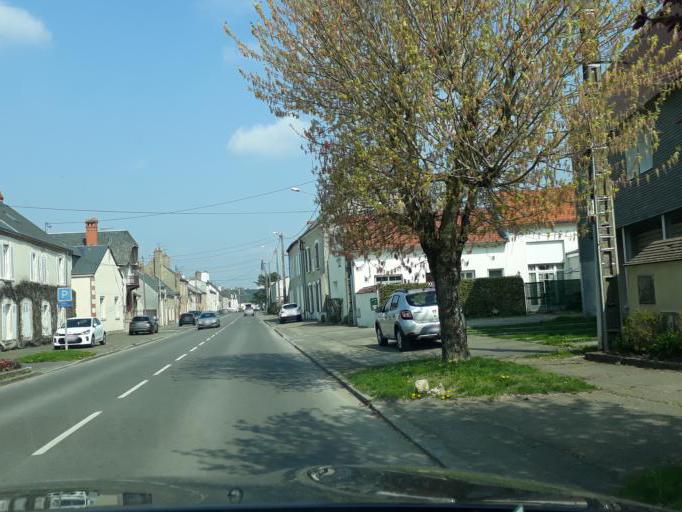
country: FR
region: Centre
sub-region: Departement du Loiret
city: Artenay
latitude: 48.0782
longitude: 1.8788
